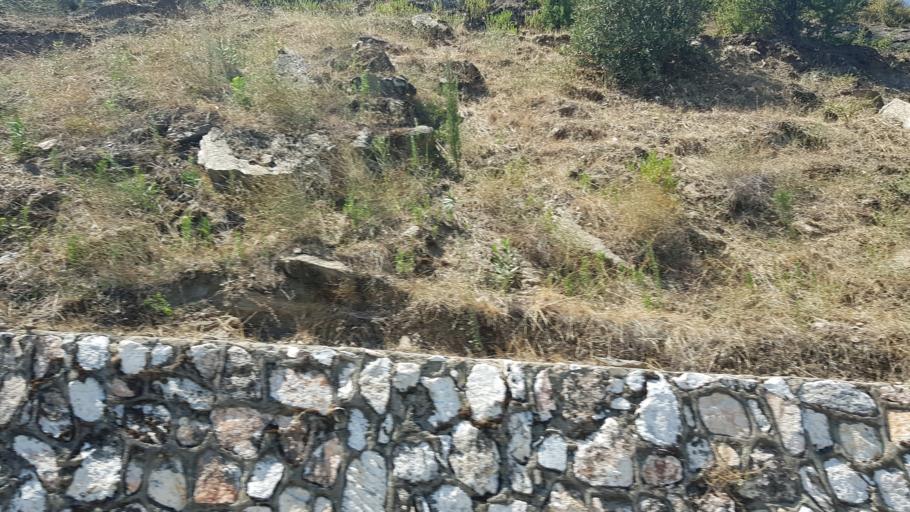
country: TR
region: Aydin
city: Akcaova
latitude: 37.5106
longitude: 28.0995
